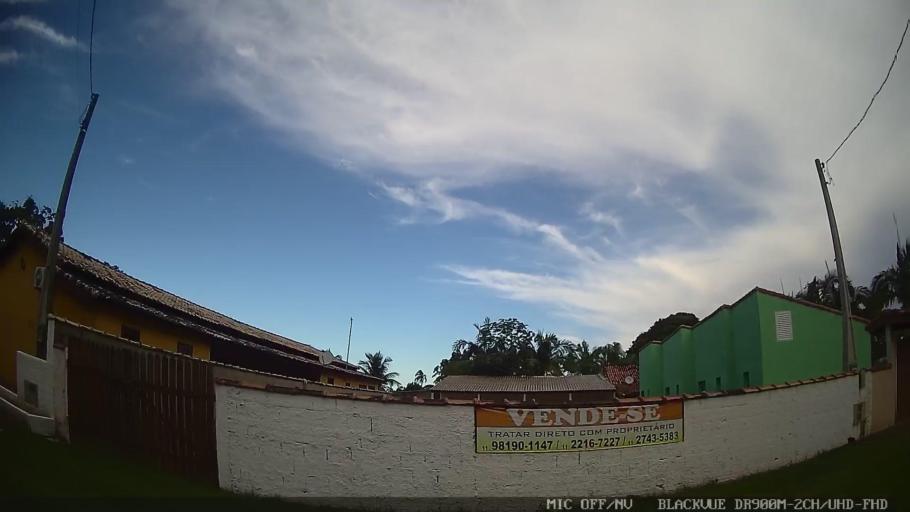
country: BR
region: Sao Paulo
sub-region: Iguape
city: Iguape
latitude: -24.6588
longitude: -47.4137
